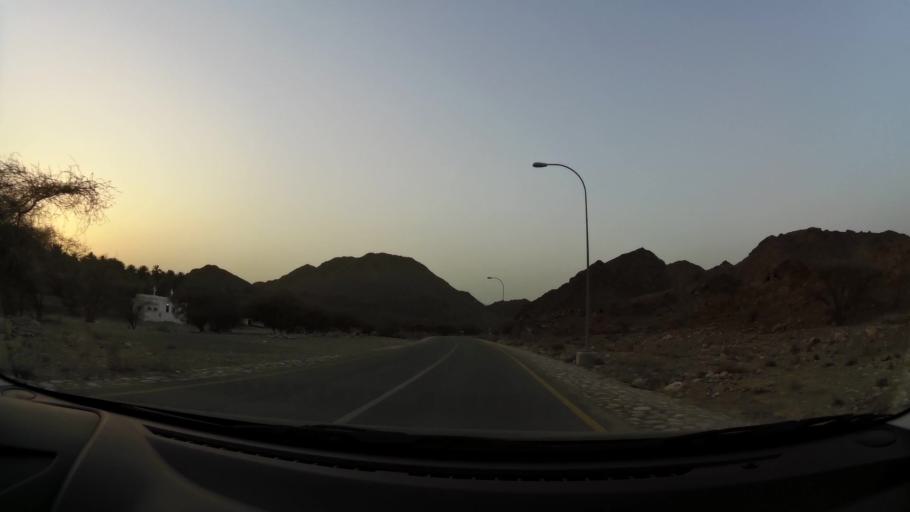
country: OM
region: Muhafazat Masqat
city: Bawshar
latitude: 23.4815
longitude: 58.3297
